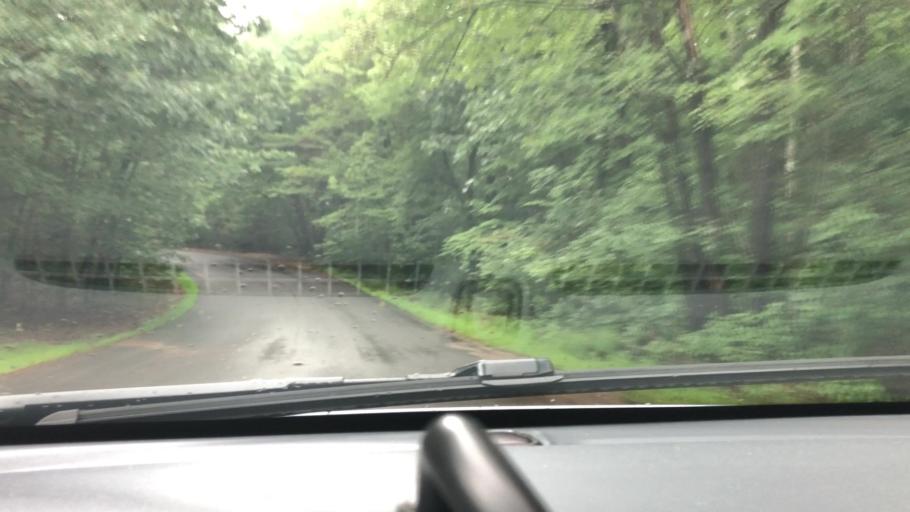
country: US
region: New Hampshire
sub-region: Hillsborough County
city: Pinardville
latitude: 43.0008
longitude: -71.4984
